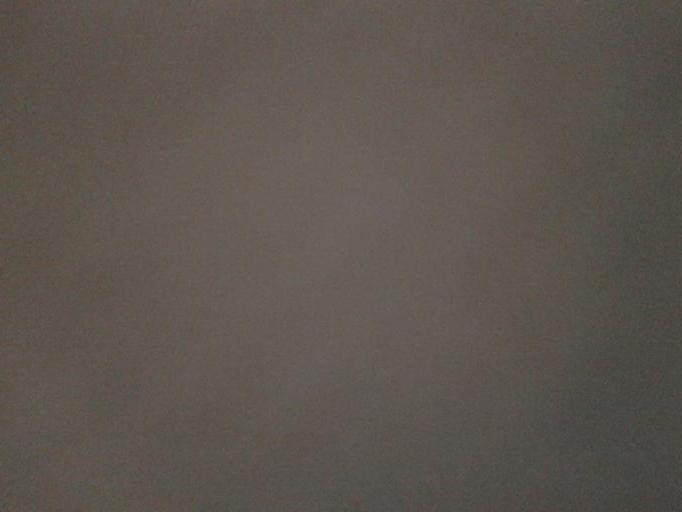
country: HT
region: Ouest
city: Tigwav
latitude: 18.3860
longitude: -72.8237
